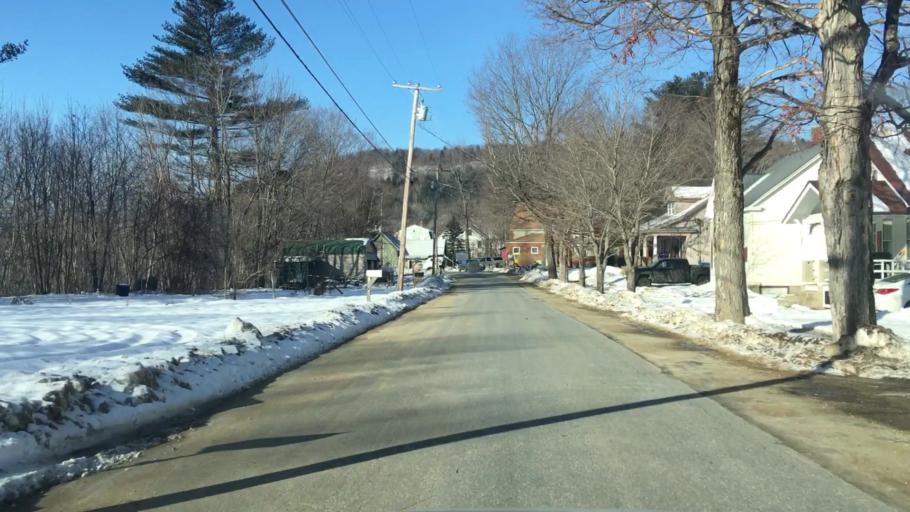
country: US
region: Maine
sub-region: Oxford County
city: West Paris
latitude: 44.3240
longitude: -70.5701
